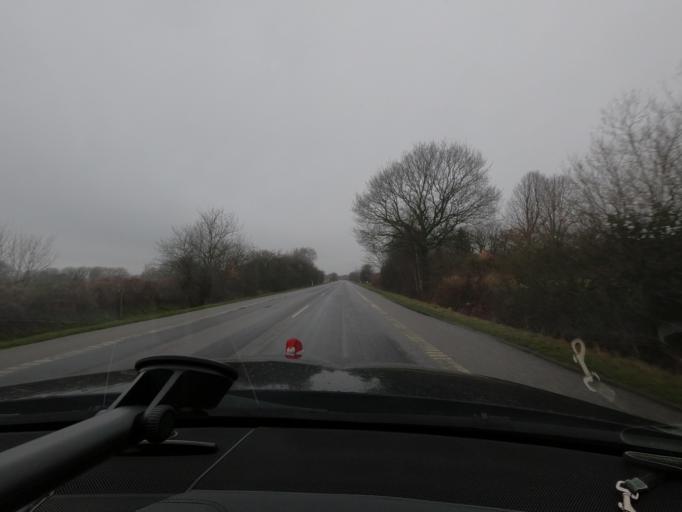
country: DK
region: South Denmark
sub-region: Sonderborg Kommune
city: Horuphav
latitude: 54.8905
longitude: 9.9732
